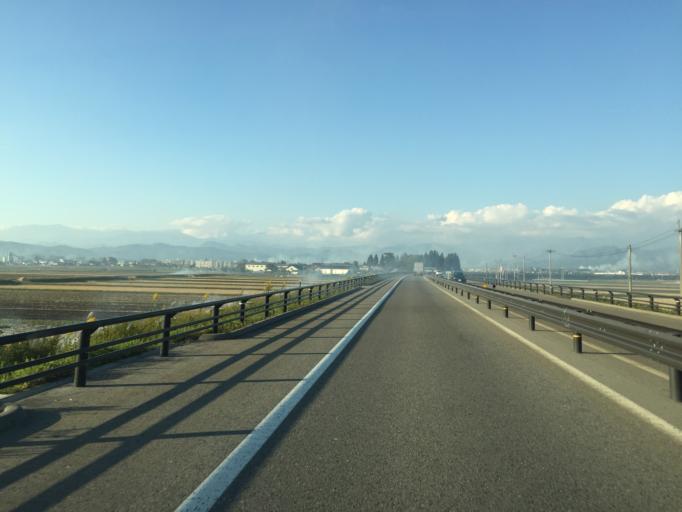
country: JP
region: Fukushima
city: Kitakata
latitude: 37.6235
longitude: 139.8811
